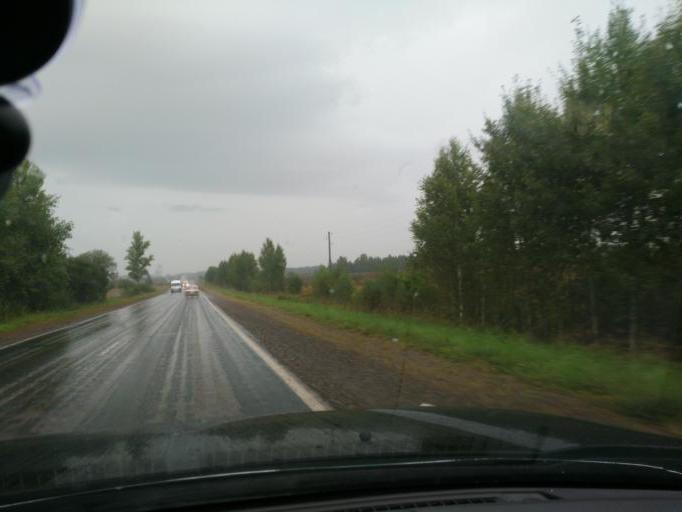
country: RU
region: Perm
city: Osa
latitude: 57.1337
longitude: 55.5265
